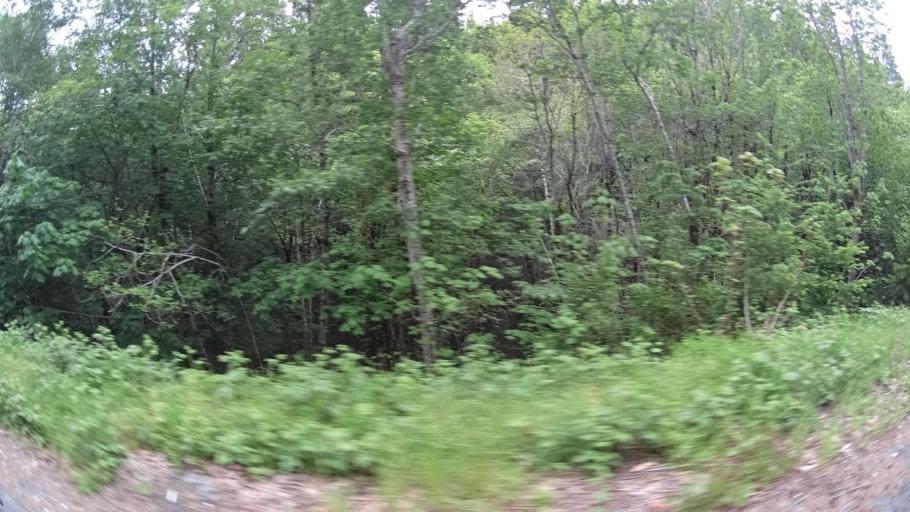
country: US
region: California
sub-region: Humboldt County
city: Blue Lake
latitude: 40.9474
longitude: -123.8443
